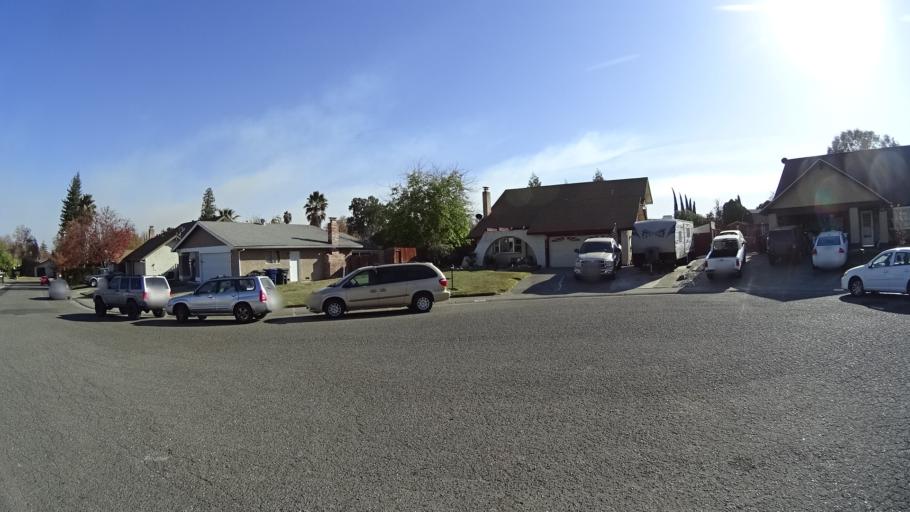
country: US
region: California
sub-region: Sacramento County
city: Antelope
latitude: 38.6997
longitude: -121.3255
